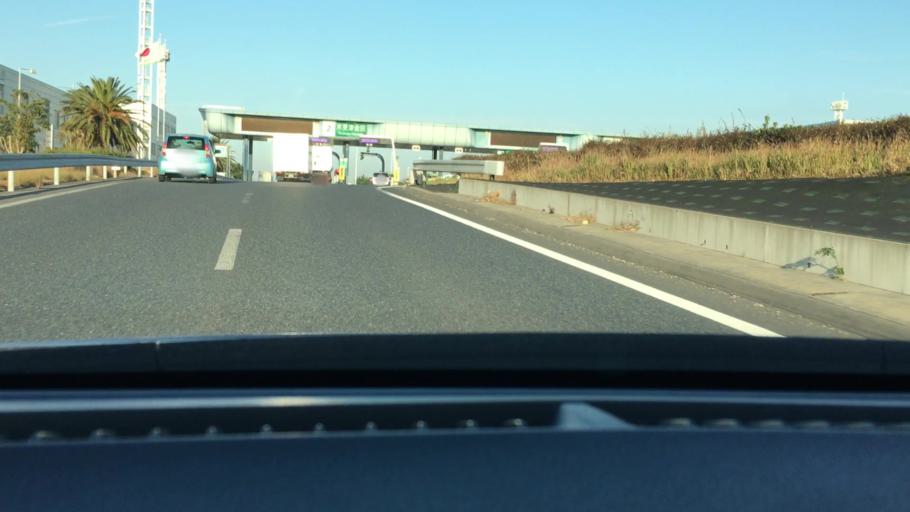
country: JP
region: Chiba
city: Kisarazu
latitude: 35.4346
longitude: 139.9197
